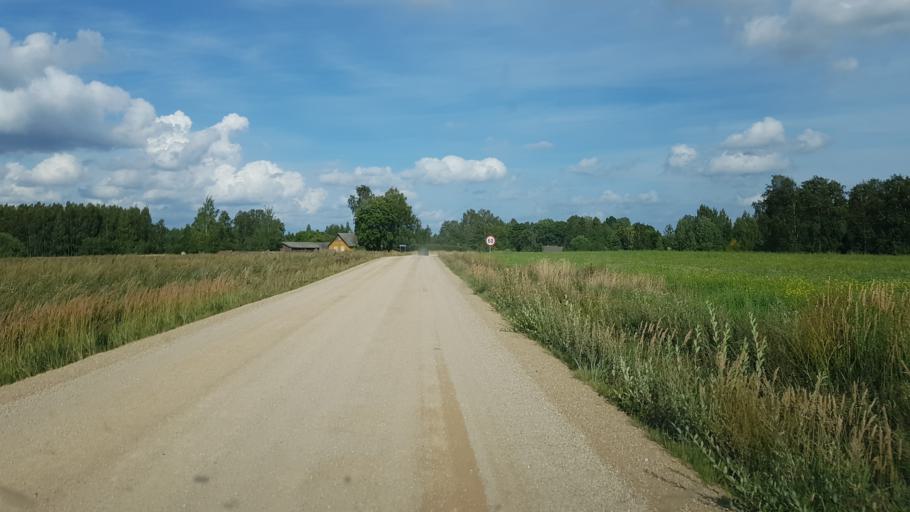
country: RU
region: Pskov
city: Pechory
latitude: 57.7961
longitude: 27.4912
